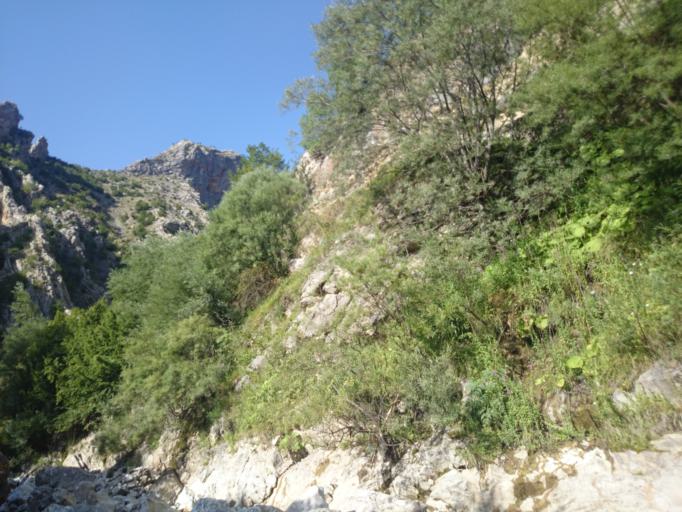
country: AL
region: Elbasan
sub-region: Rrethi i Gramshit
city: Lenias
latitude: 40.7847
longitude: 20.3908
